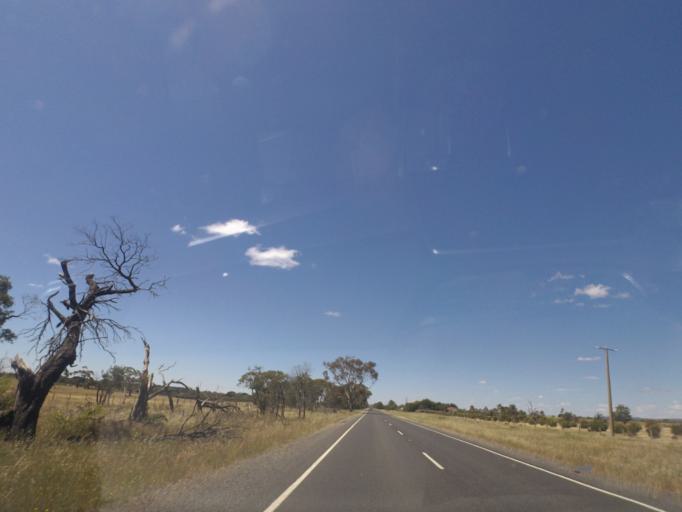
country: AU
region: Victoria
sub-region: Mount Alexander
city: Castlemaine
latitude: -37.2213
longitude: 144.3425
